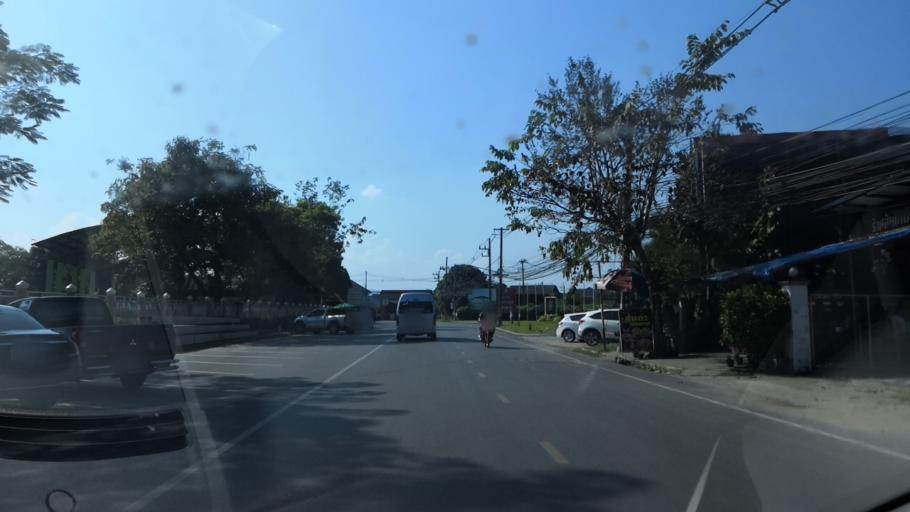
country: TH
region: Chiang Rai
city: Chiang Rai
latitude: 19.9288
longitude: 99.8521
